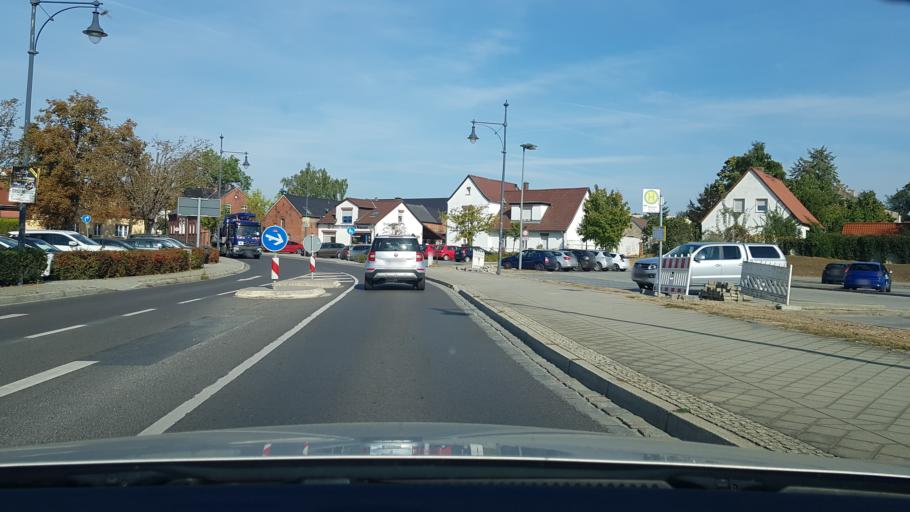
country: DE
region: Brandenburg
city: Beeskow
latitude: 52.1729
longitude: 14.2516
